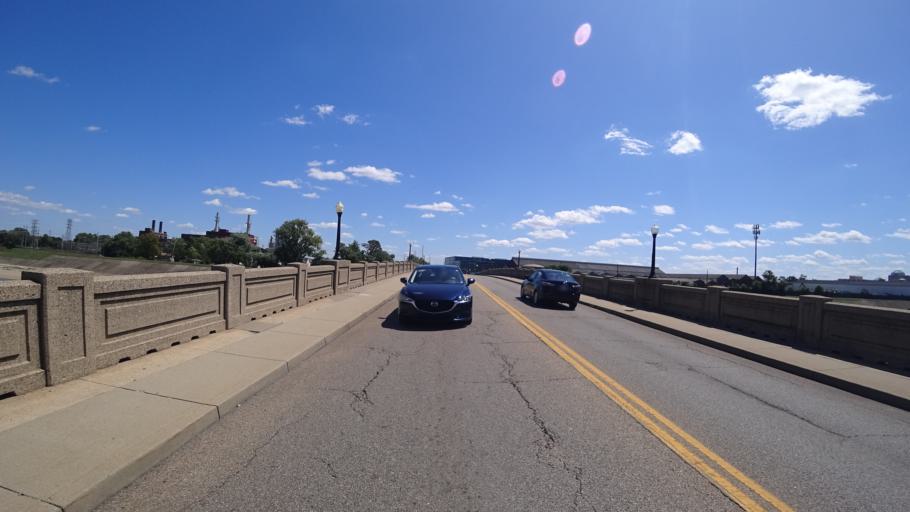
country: US
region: Ohio
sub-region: Butler County
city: Hamilton
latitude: 39.4098
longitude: -84.5593
